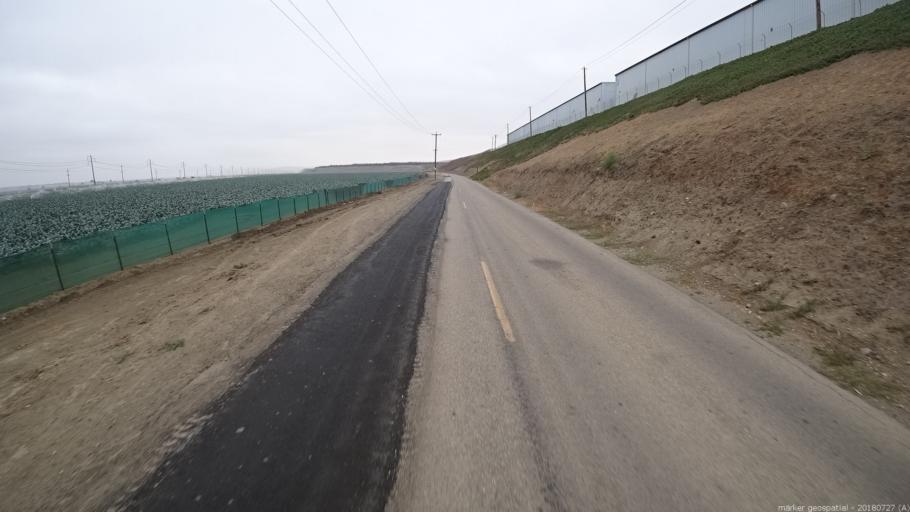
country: US
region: California
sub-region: Monterey County
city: King City
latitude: 36.2296
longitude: -121.1291
